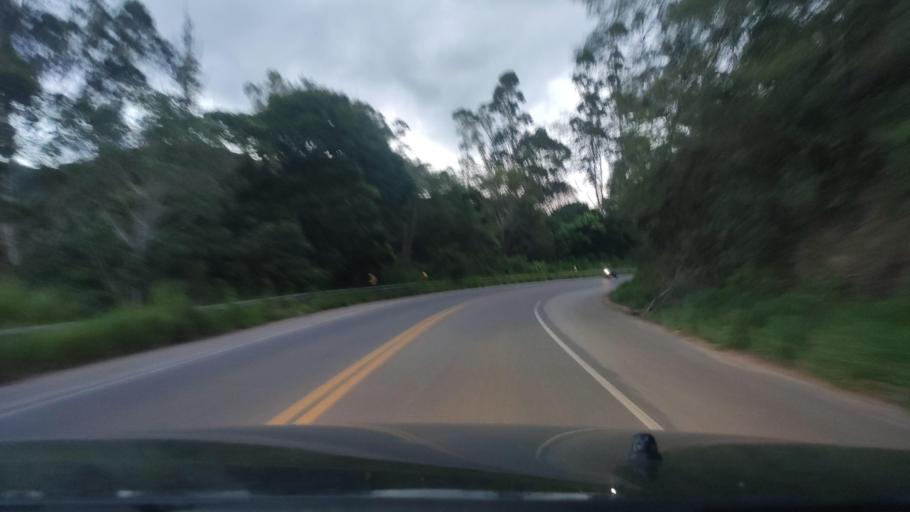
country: BR
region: Sao Paulo
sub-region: Campos Do Jordao
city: Campos do Jordao
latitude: -22.7771
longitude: -45.7438
